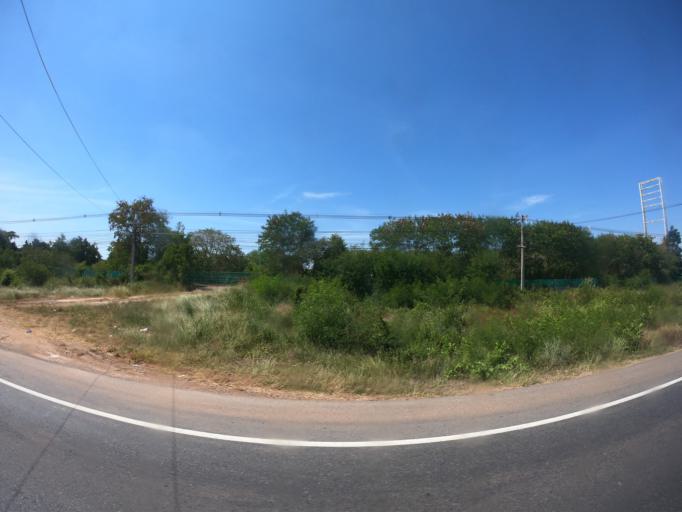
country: TH
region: Khon Kaen
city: Ban Phai
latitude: 16.0235
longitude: 102.7088
